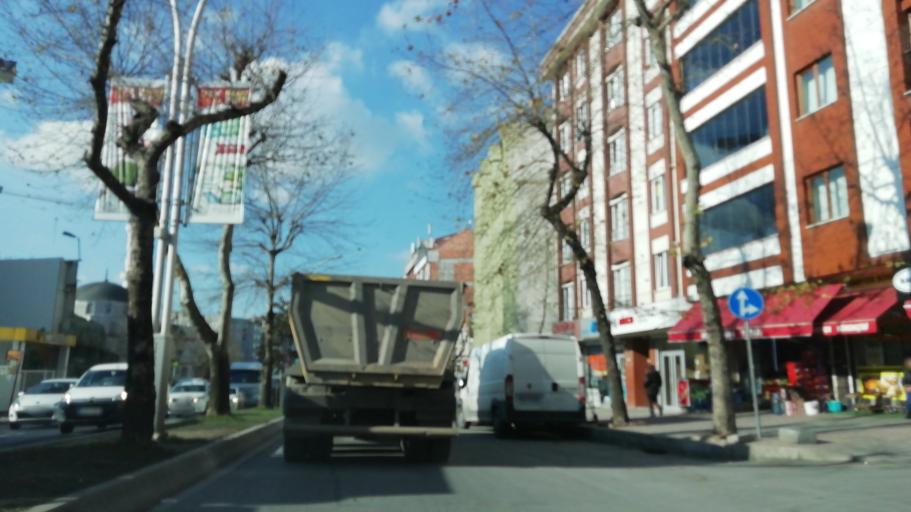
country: TR
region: Istanbul
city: Esenler
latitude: 41.0599
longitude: 28.9061
